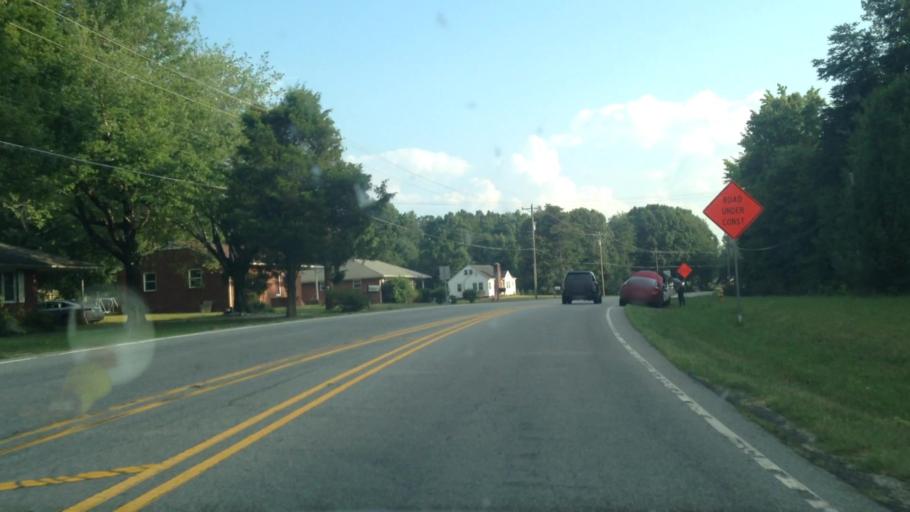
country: US
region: North Carolina
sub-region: Forsyth County
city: Kernersville
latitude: 36.0388
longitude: -80.0504
